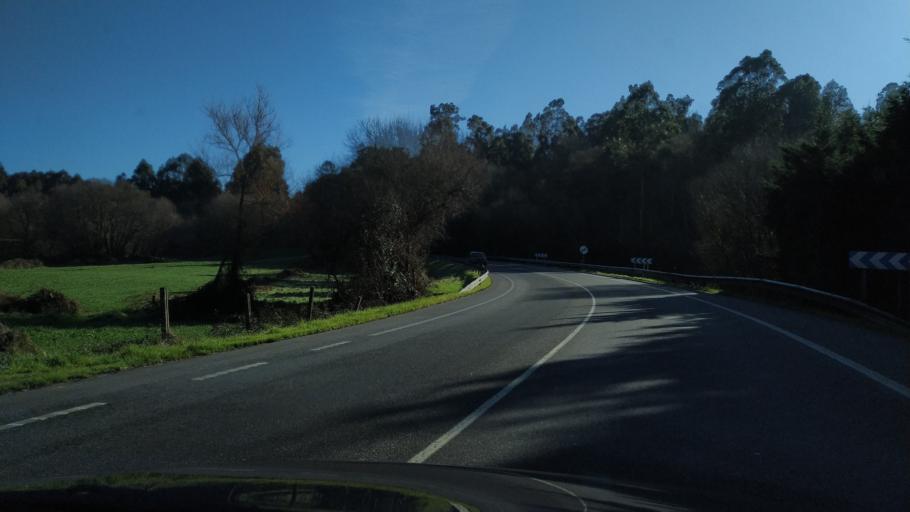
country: ES
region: Galicia
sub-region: Provincia de Pontevedra
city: Silleda
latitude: 42.7299
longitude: -8.3174
